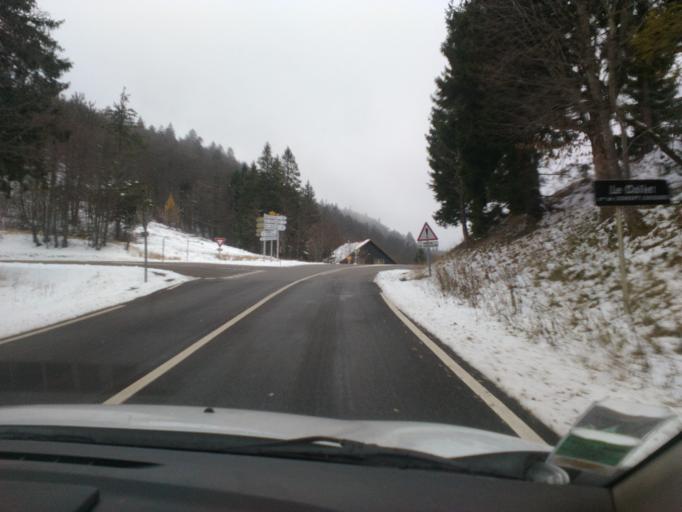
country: FR
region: Alsace
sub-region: Departement du Haut-Rhin
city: Metzeral
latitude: 48.0538
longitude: 7.0048
